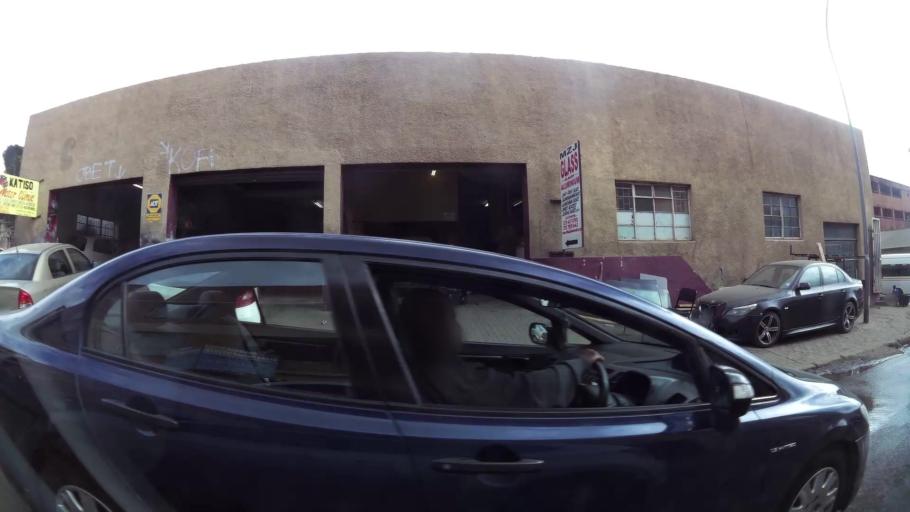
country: ZA
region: Orange Free State
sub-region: Mangaung Metropolitan Municipality
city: Bloemfontein
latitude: -29.1225
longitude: 26.2231
